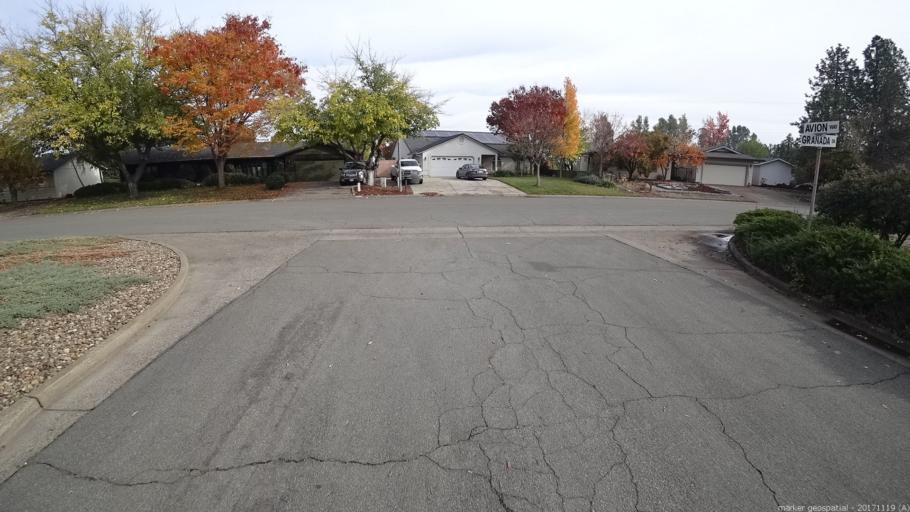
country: US
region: California
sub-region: Shasta County
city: Anderson
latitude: 40.4889
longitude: -122.3068
